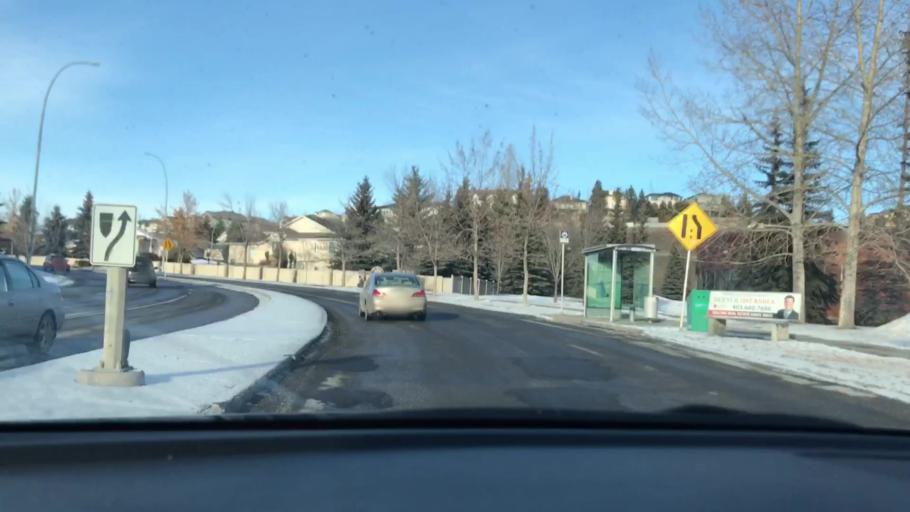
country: CA
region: Alberta
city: Calgary
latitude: 51.0182
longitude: -114.1760
